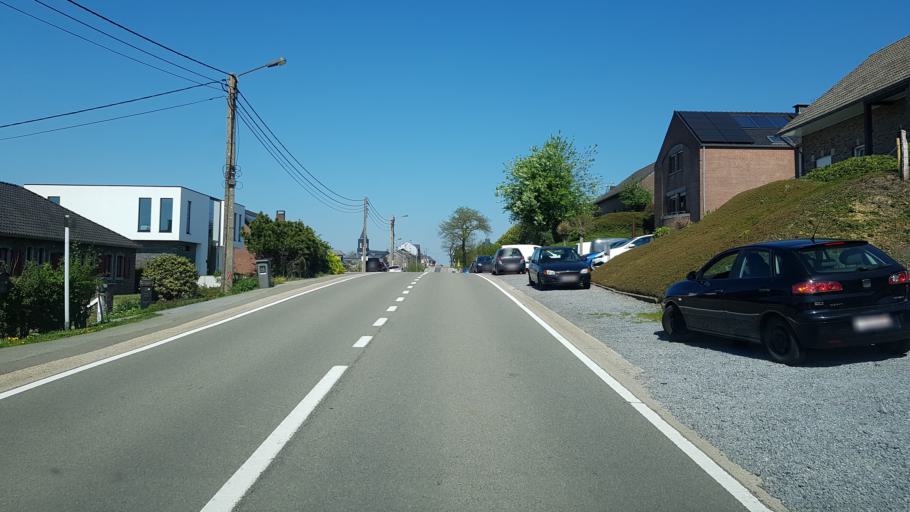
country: BE
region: Wallonia
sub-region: Province de Liege
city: Plombieres
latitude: 50.7193
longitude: 5.9175
